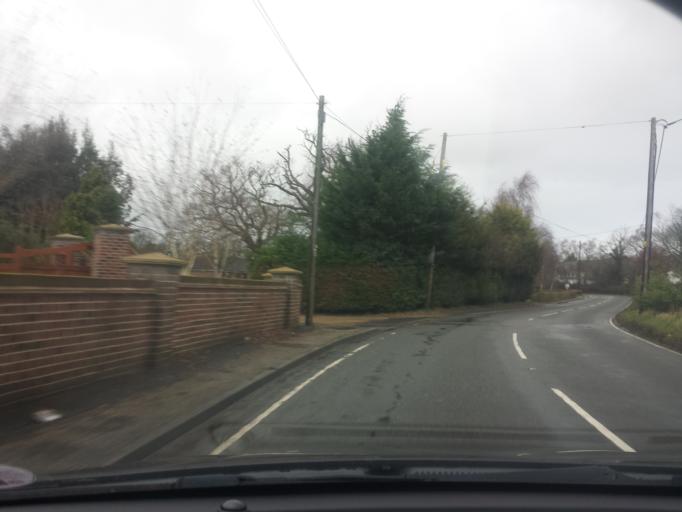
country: GB
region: England
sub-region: Essex
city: Mistley
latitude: 51.8935
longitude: 1.1026
